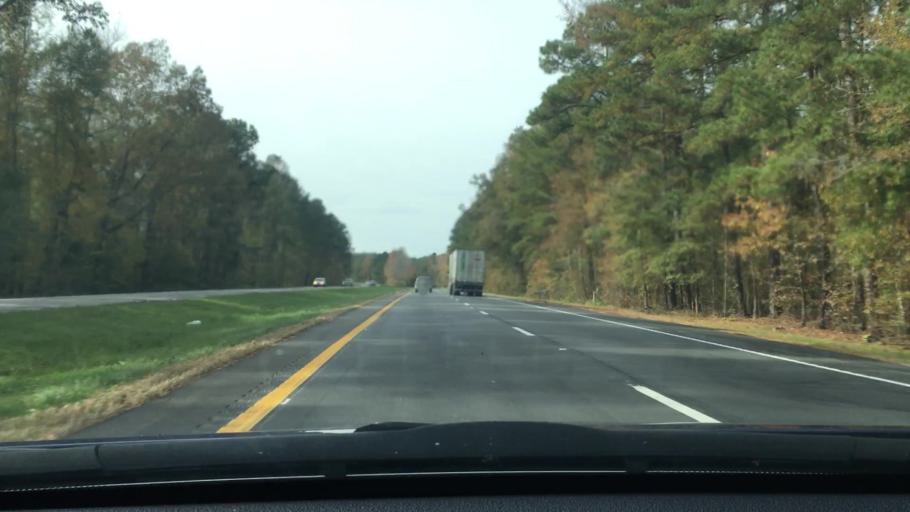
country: US
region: South Carolina
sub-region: Sumter County
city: Stateburg
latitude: 33.9516
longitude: -80.5589
